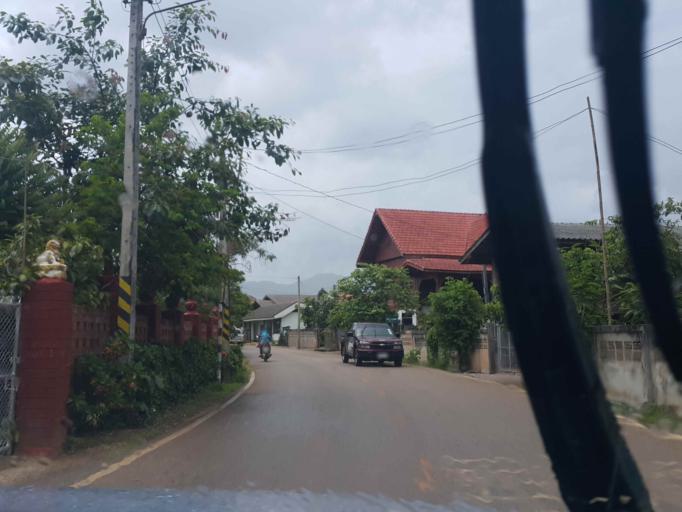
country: TH
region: Phayao
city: Dok Kham Tai
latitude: 19.0596
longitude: 100.0321
